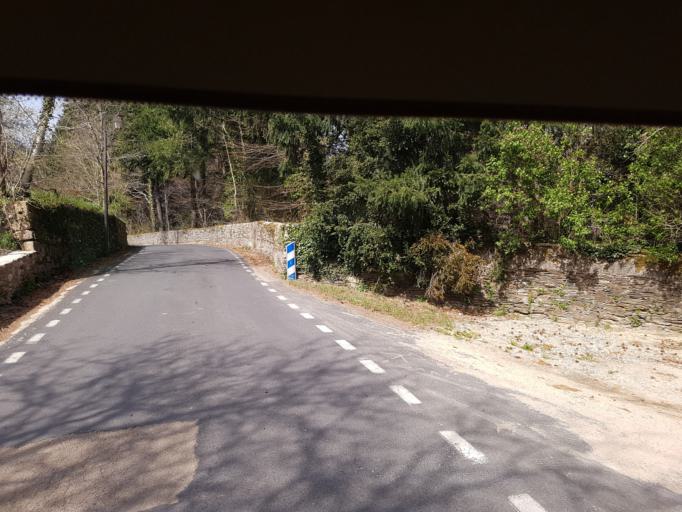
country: FR
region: Languedoc-Roussillon
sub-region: Departement de la Lozere
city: Florac
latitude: 44.2564
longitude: 3.5830
